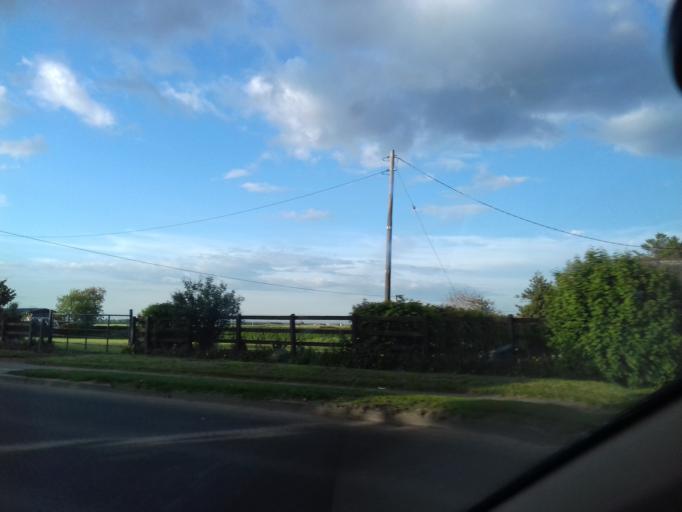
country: IE
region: Leinster
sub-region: South Dublin
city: Rathcoole
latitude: 53.2876
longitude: -6.4639
